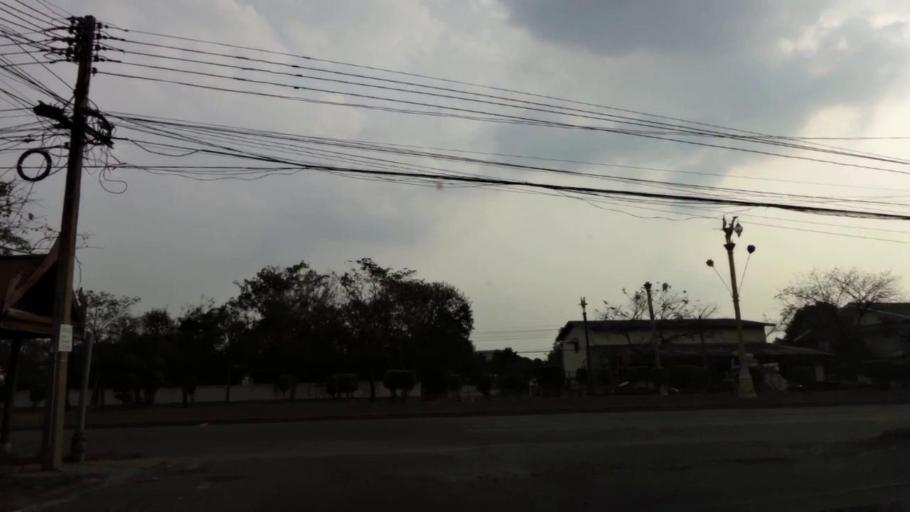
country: TH
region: Phra Nakhon Si Ayutthaya
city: Phra Nakhon Si Ayutthaya
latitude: 14.3515
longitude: 100.5735
